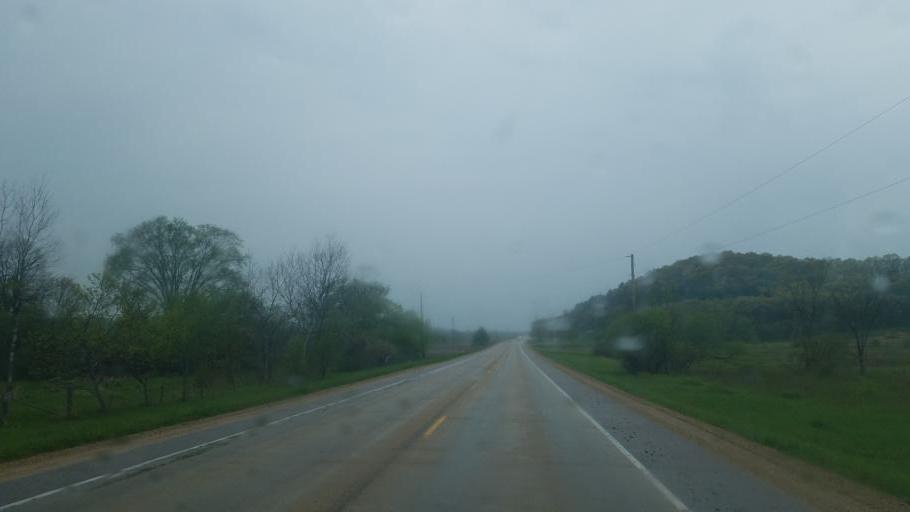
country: US
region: Wisconsin
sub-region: Sauk County
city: Reedsburg
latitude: 43.6181
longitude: -90.1487
